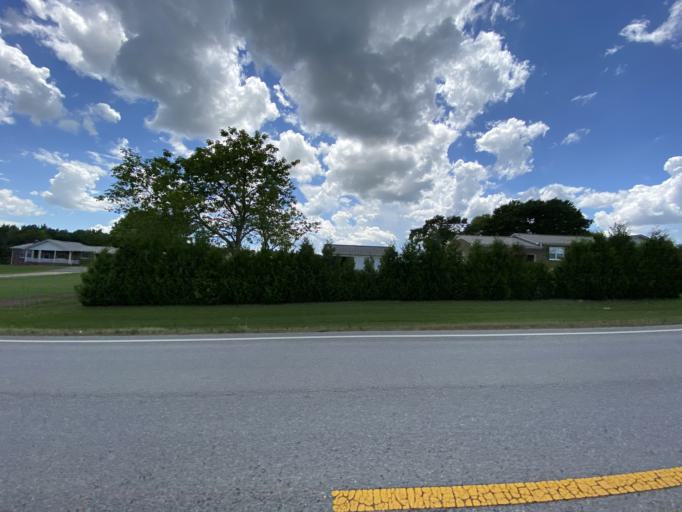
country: US
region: Alabama
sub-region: Lauderdale County
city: Underwood-Petersville
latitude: 34.9403
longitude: -87.8564
